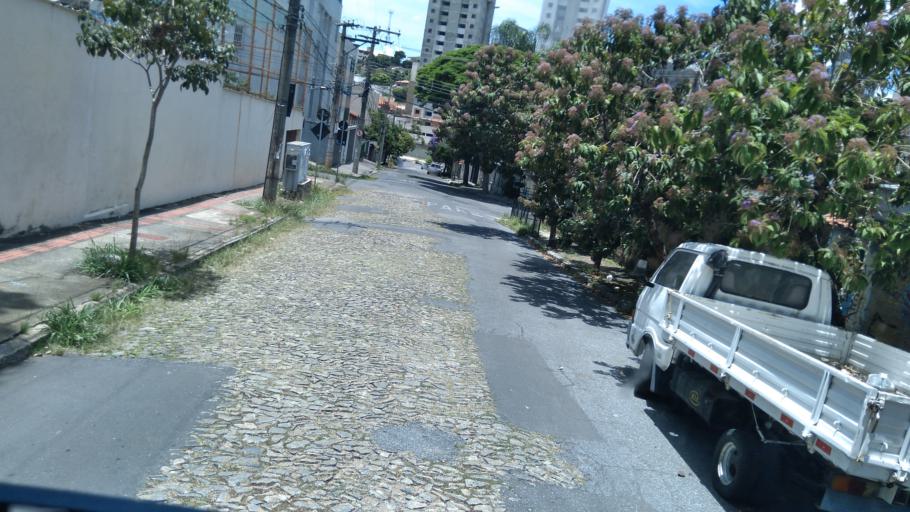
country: BR
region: Minas Gerais
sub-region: Belo Horizonte
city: Belo Horizonte
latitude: -19.9198
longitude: -43.9883
